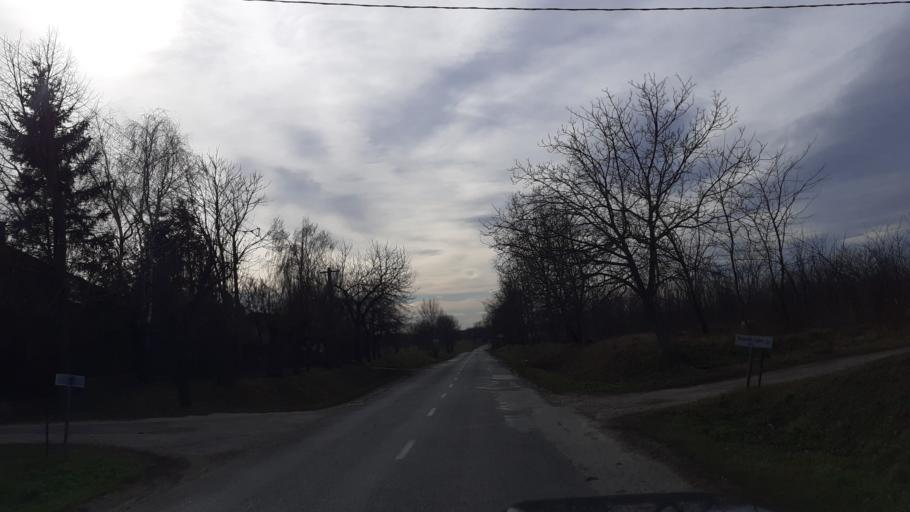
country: HU
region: Fejer
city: Sarbogard
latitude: 46.9263
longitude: 18.6808
